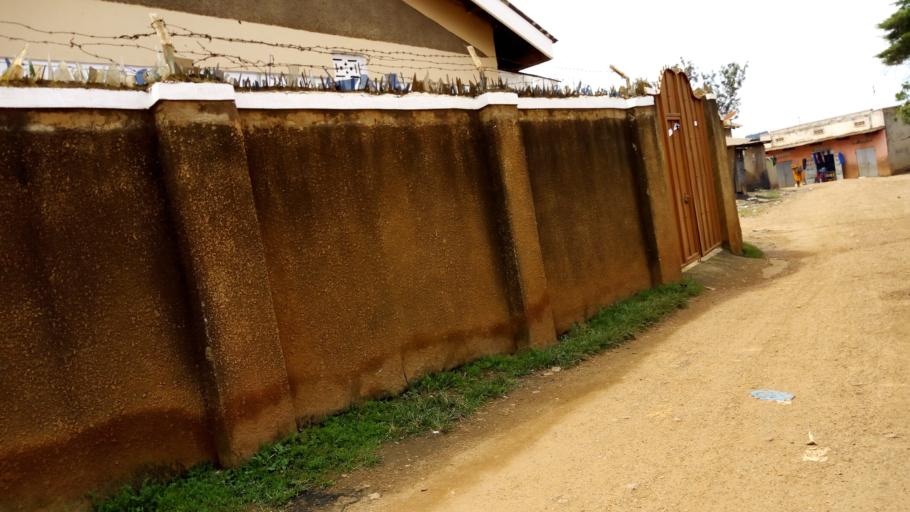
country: UG
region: Central Region
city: Kampala Central Division
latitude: 0.3762
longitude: 32.5618
